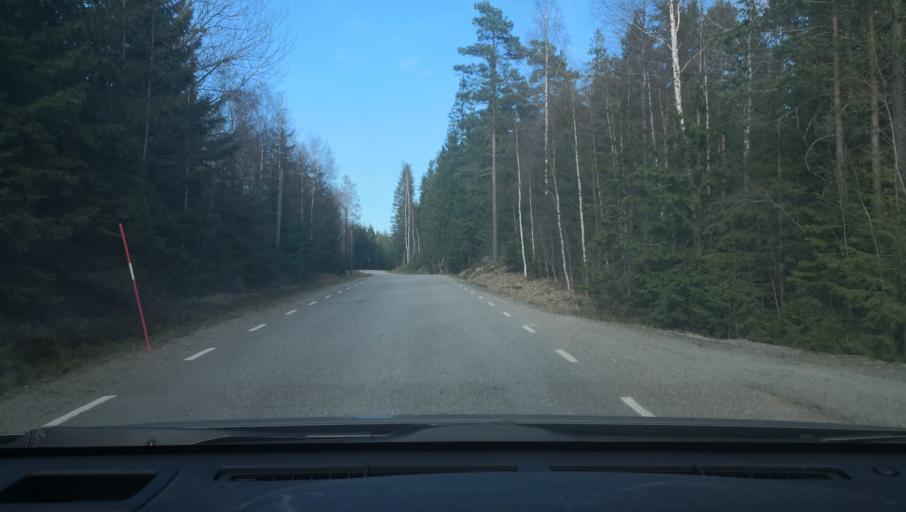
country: SE
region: Uppsala
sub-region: Heby Kommun
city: Heby
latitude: 59.9148
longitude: 16.8337
